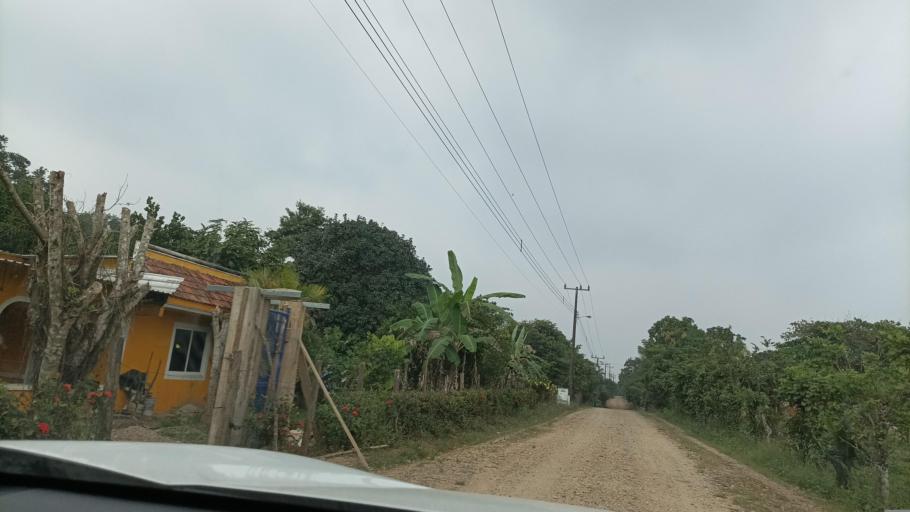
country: MX
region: Veracruz
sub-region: Uxpanapa
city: Poblado 10
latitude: 17.5510
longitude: -94.2243
